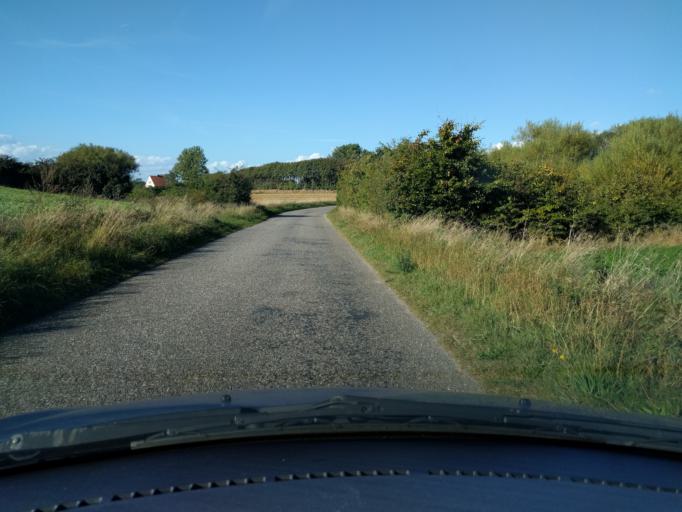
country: DK
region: South Denmark
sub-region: Assens Kommune
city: Harby
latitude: 55.1312
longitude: 10.0310
